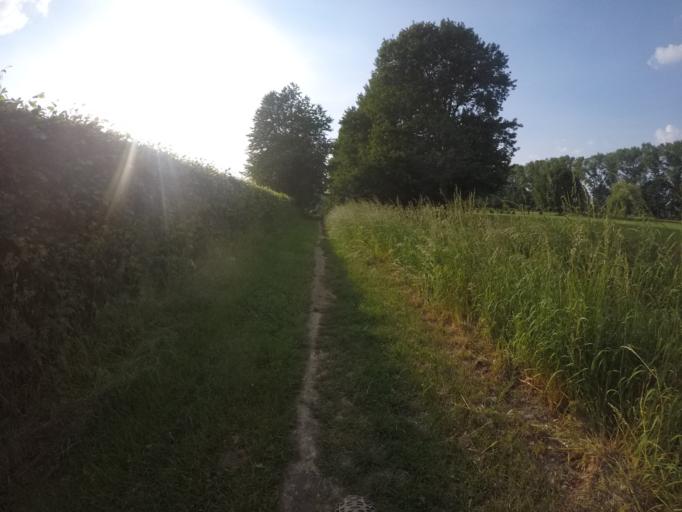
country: DE
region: North Rhine-Westphalia
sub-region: Regierungsbezirk Munster
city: Isselburg
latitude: 51.8360
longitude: 6.4395
